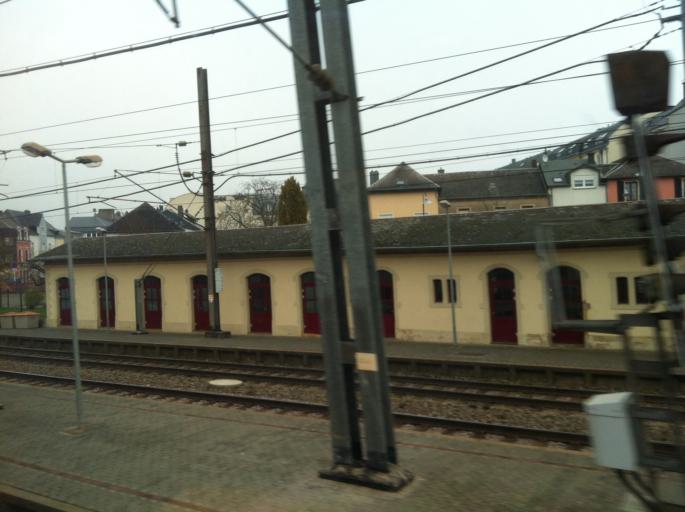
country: LU
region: Luxembourg
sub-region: Canton d'Esch-sur-Alzette
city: Bettembourg
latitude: 49.5170
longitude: 6.1016
